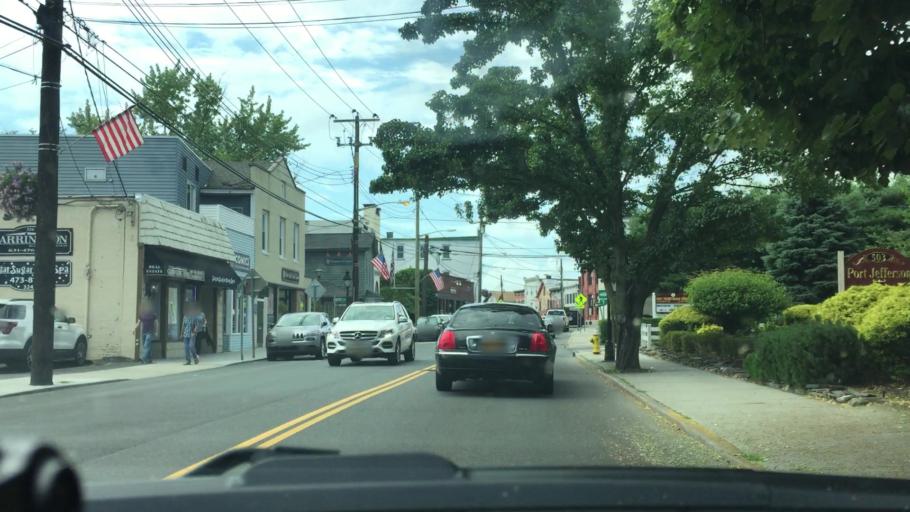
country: US
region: New York
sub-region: Suffolk County
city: Port Jefferson
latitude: 40.9442
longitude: -73.0675
